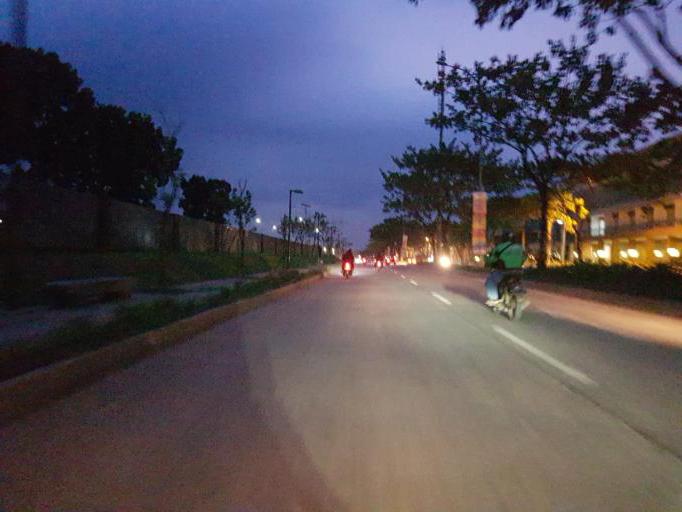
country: ID
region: West Java
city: Serpong
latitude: -6.3177
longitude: 106.6486
